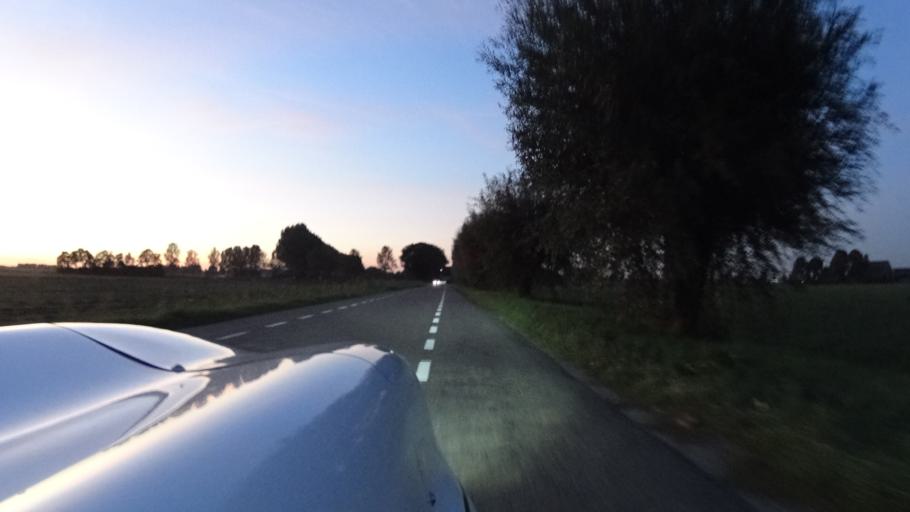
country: NL
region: North Brabant
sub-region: Gemeente Aalburg
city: Aalburg
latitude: 51.7550
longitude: 5.0813
